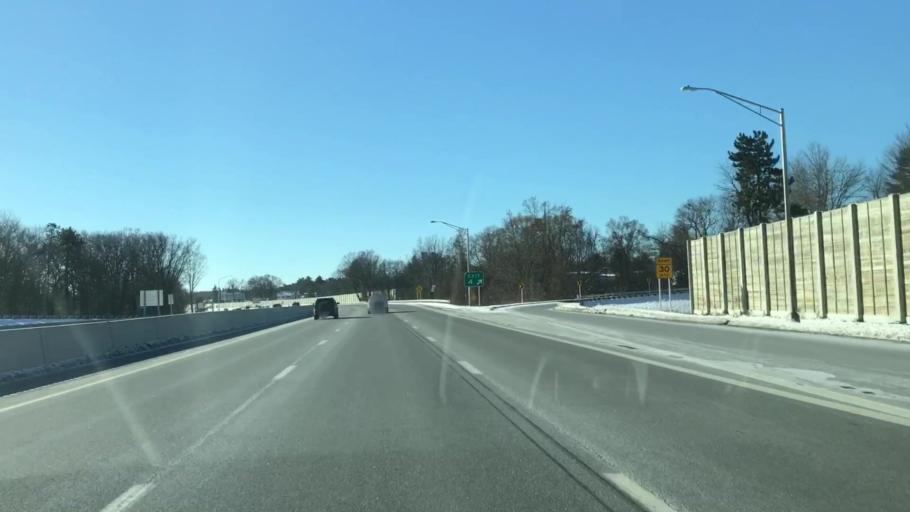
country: US
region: New Hampshire
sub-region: Hillsborough County
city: Manchester
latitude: 42.9725
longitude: -71.4749
